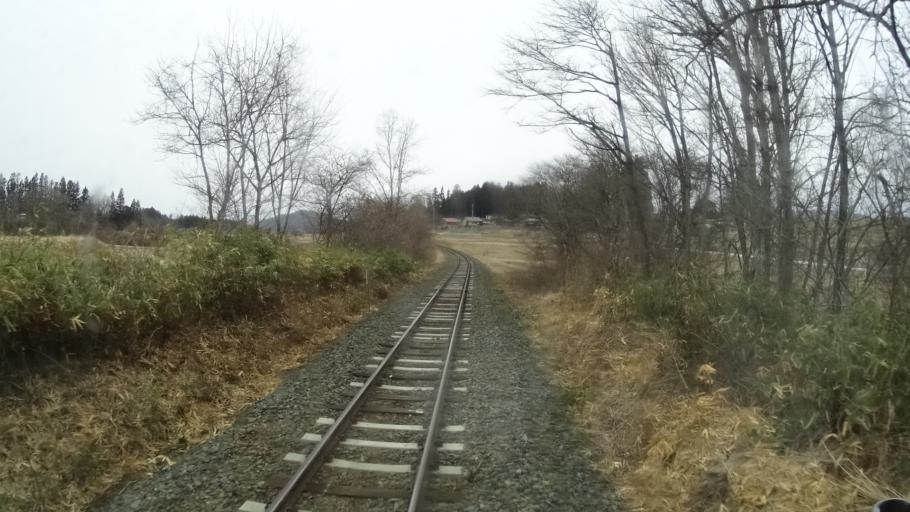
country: JP
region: Iwate
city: Hanamaki
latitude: 39.3964
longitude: 141.2115
